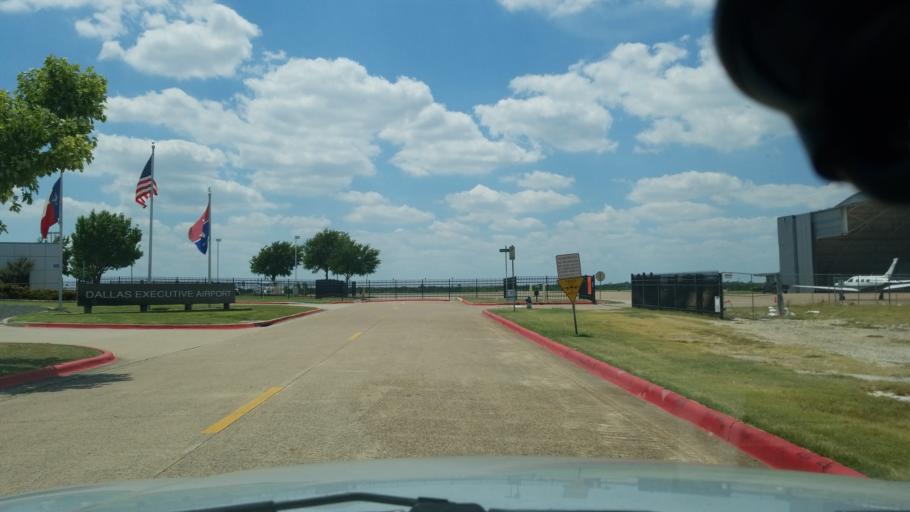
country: US
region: Texas
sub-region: Dallas County
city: Duncanville
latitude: 32.6815
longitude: -96.8640
